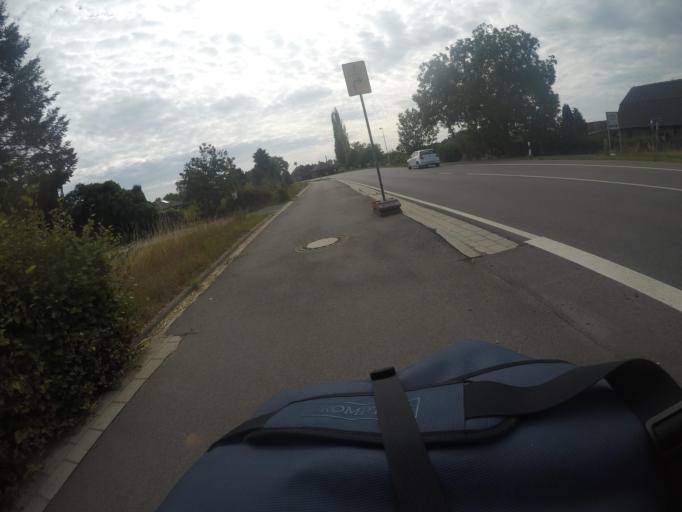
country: DE
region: North Rhine-Westphalia
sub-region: Regierungsbezirk Dusseldorf
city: Emmerich
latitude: 51.8442
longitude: 6.2126
